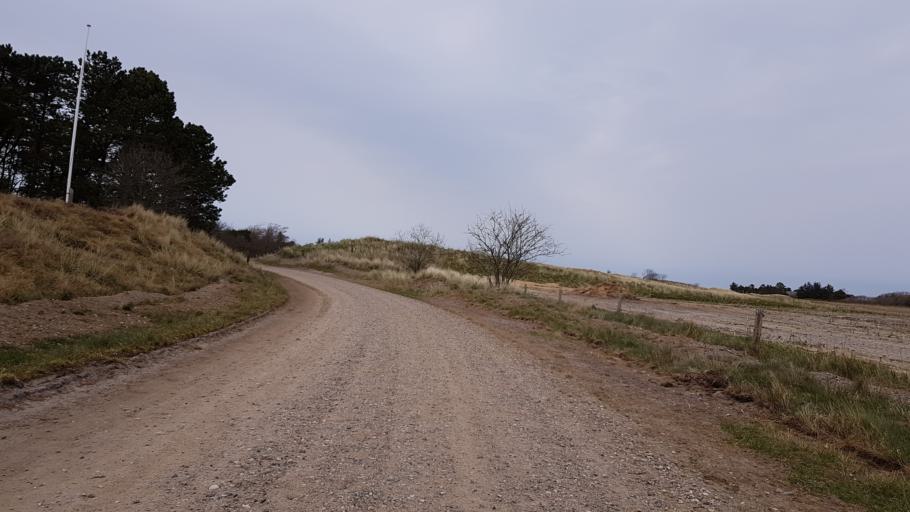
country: DE
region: Schleswig-Holstein
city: List
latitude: 55.1689
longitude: 8.5509
